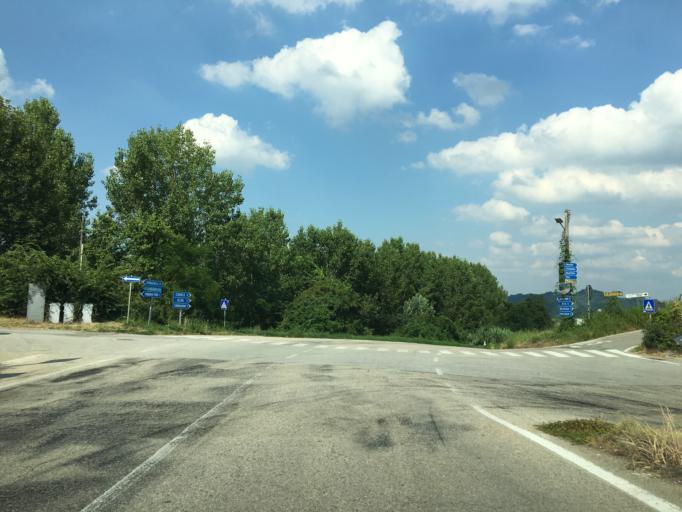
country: IT
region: Piedmont
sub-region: Provincia di Cuneo
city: Sommariva Perno
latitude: 44.7399
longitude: 7.9099
